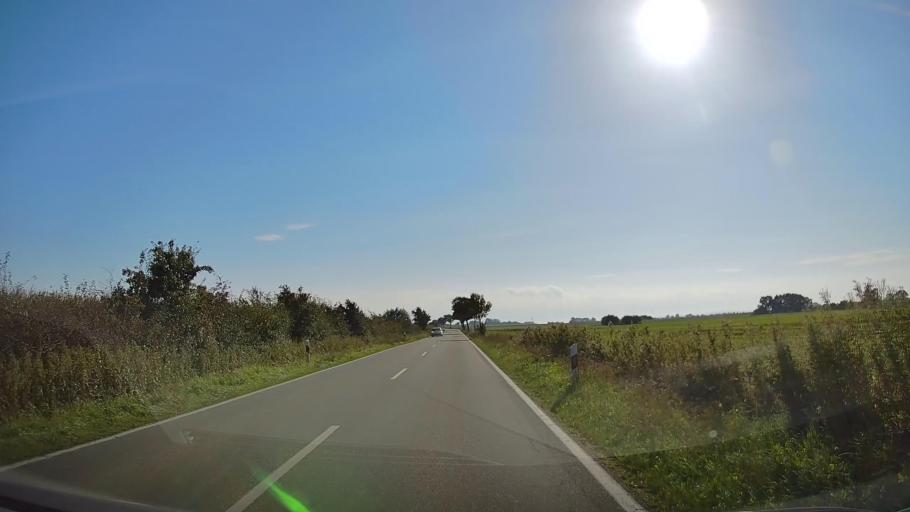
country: DE
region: Schleswig-Holstein
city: Fehmarn
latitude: 54.4408
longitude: 11.1382
